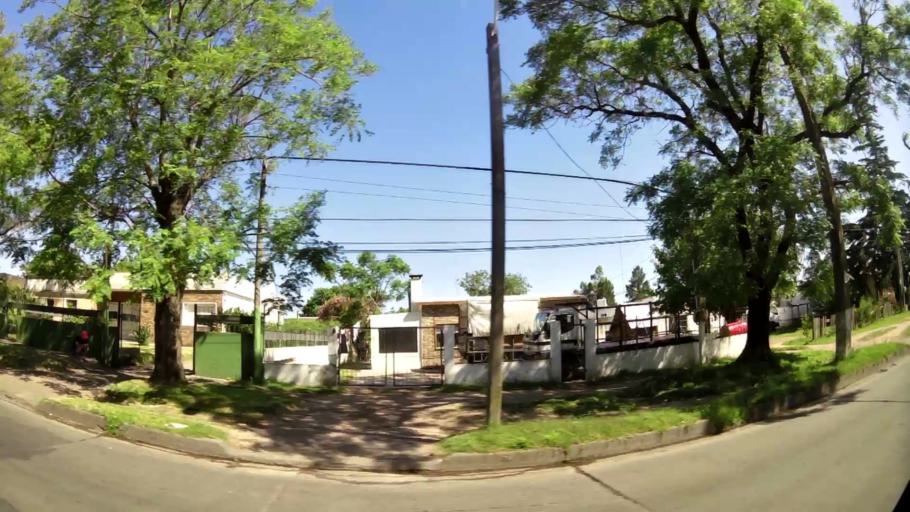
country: UY
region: Montevideo
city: Pajas Blancas
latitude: -34.8378
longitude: -56.2625
